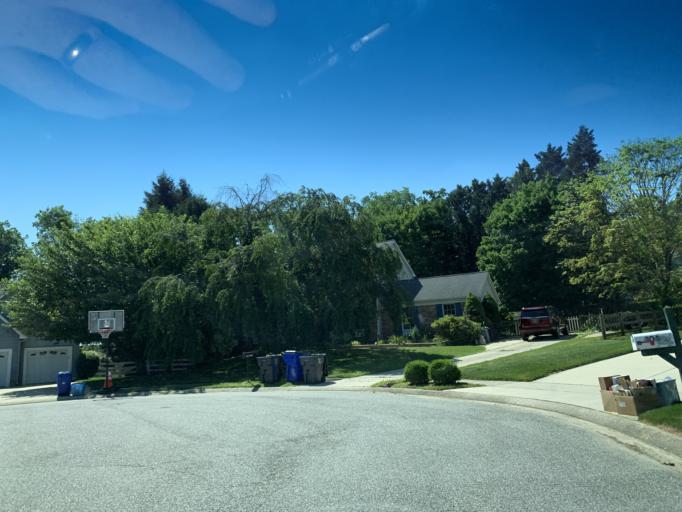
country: US
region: Maryland
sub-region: Harford County
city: South Bel Air
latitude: 39.5268
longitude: -76.3198
